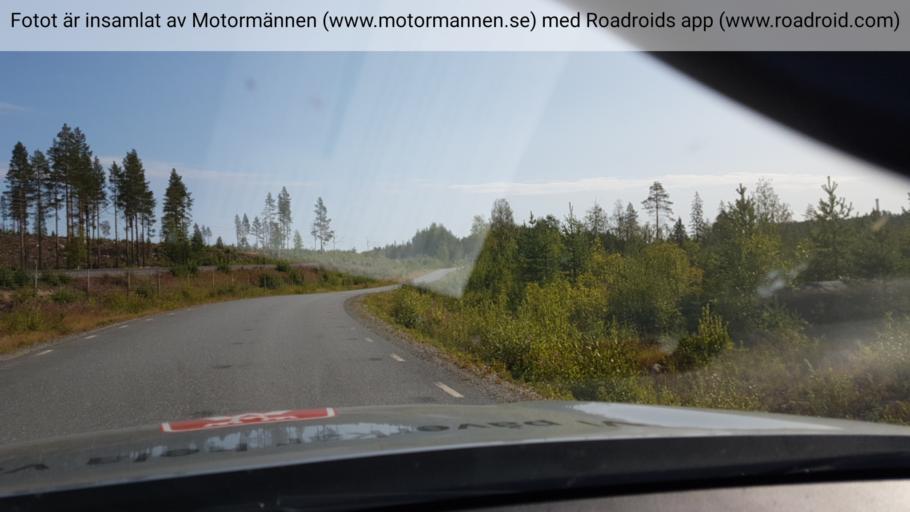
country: SE
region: Norrbotten
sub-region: Alvsbyns Kommun
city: AElvsbyn
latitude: 65.5834
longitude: 20.6310
